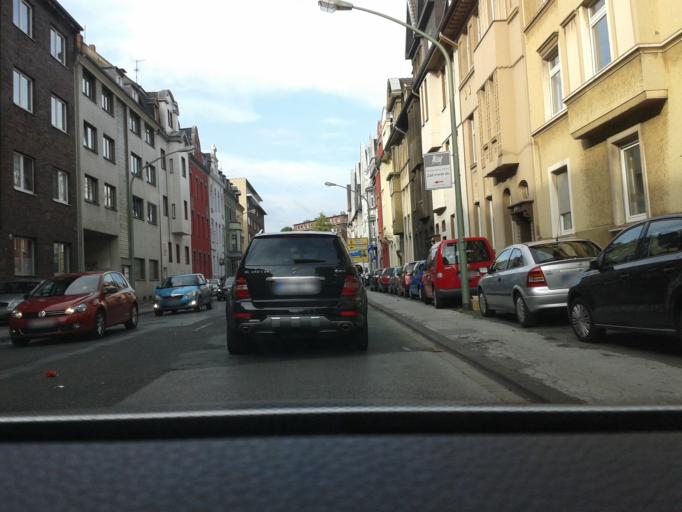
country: DE
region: North Rhine-Westphalia
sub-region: Regierungsbezirk Dusseldorf
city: Duisburg
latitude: 51.4319
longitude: 6.7956
